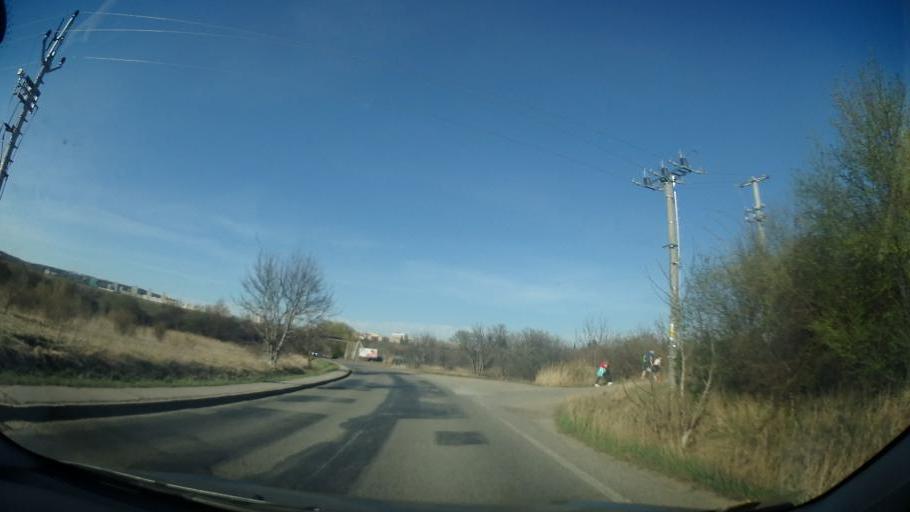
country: CZ
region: South Moravian
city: Ostopovice
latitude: 49.1607
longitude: 16.5527
